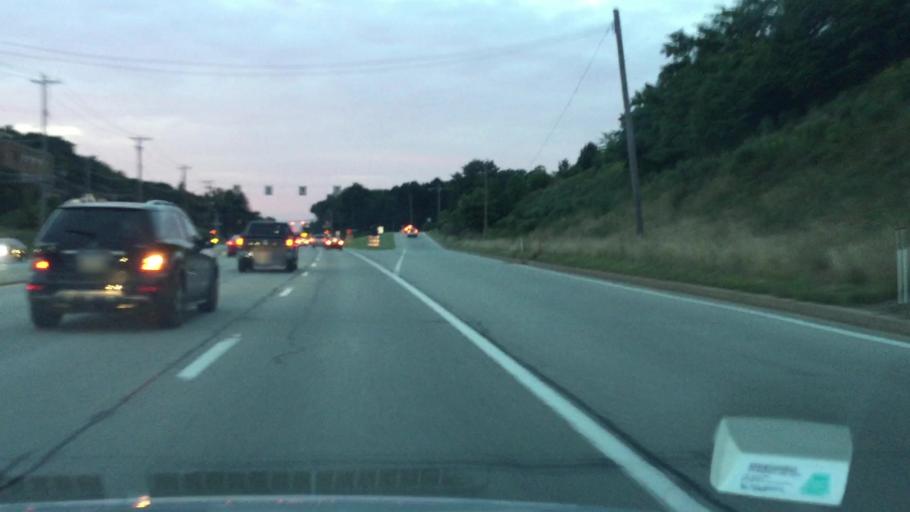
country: US
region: Pennsylvania
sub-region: Allegheny County
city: West View
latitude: 40.5522
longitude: -80.0196
